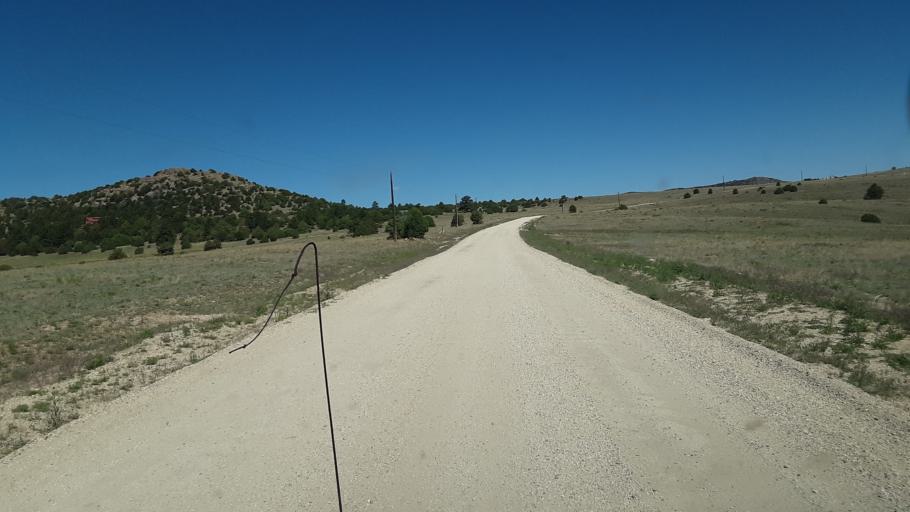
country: US
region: Colorado
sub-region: Custer County
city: Westcliffe
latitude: 38.2194
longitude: -105.4542
